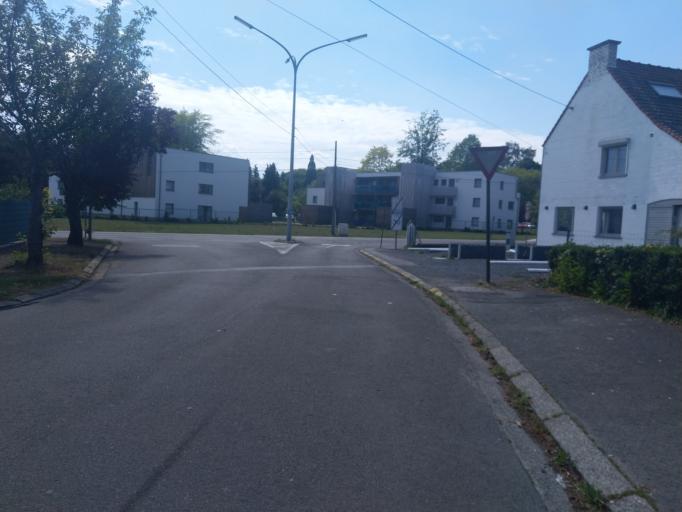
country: BE
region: Wallonia
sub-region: Province du Hainaut
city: Mons
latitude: 50.4486
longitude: 3.9923
